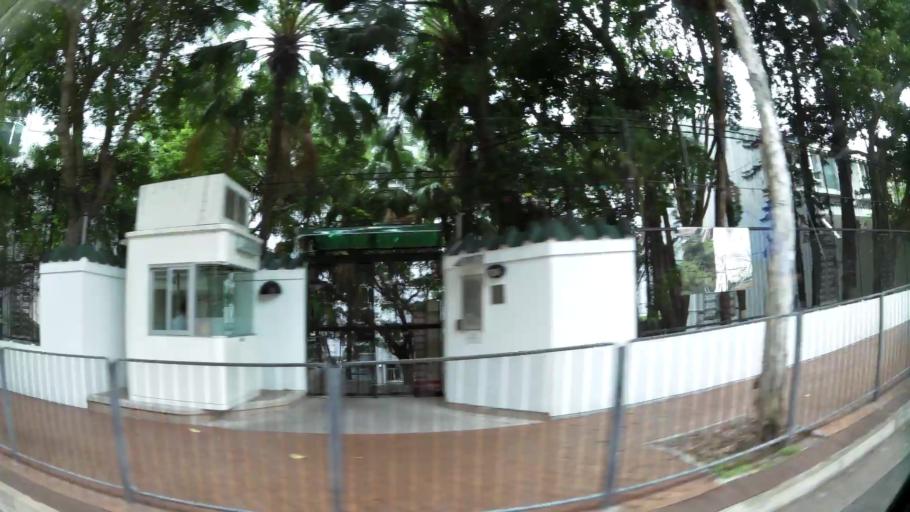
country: HK
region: Sham Shui Po
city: Sham Shui Po
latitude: 22.3343
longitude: 114.1756
